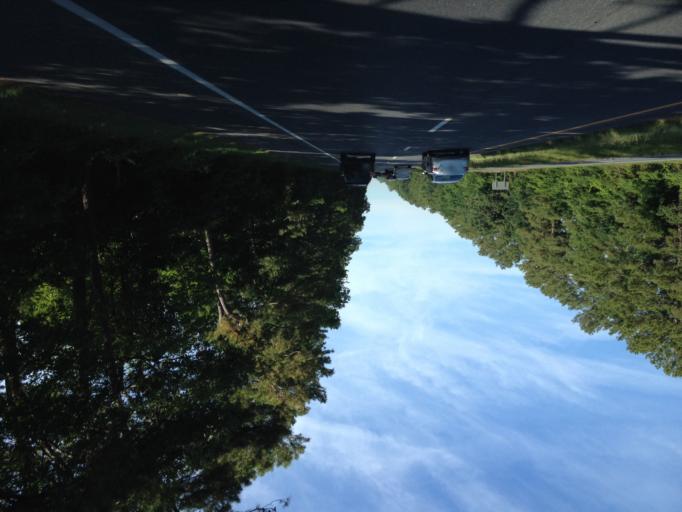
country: US
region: Delaware
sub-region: Sussex County
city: Millsboro
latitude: 38.6061
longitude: -75.3238
